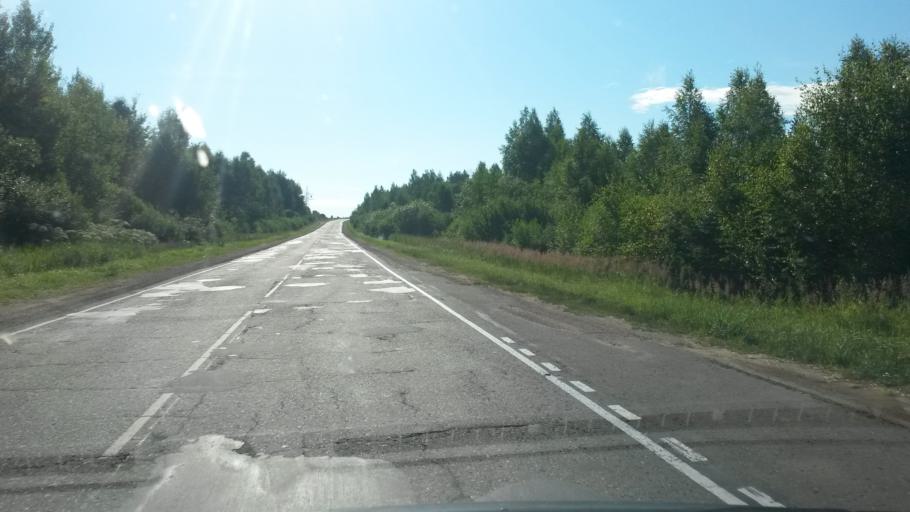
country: RU
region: Ivanovo
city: Pistsovo
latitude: 57.1878
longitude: 40.4439
